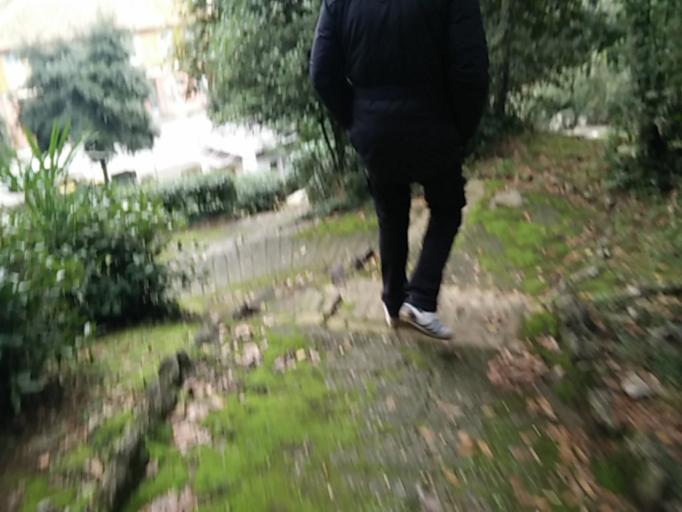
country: HR
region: Primorsko-Goranska
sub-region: Grad Opatija
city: Opatija
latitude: 45.3332
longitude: 14.3011
